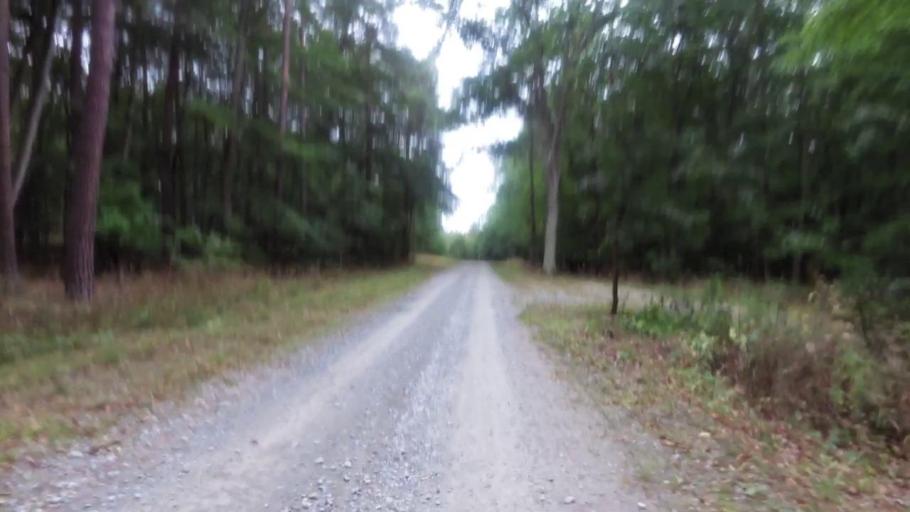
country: PL
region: Lubusz
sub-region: Powiat gorzowski
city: Kostrzyn nad Odra
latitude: 52.6248
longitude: 14.6487
